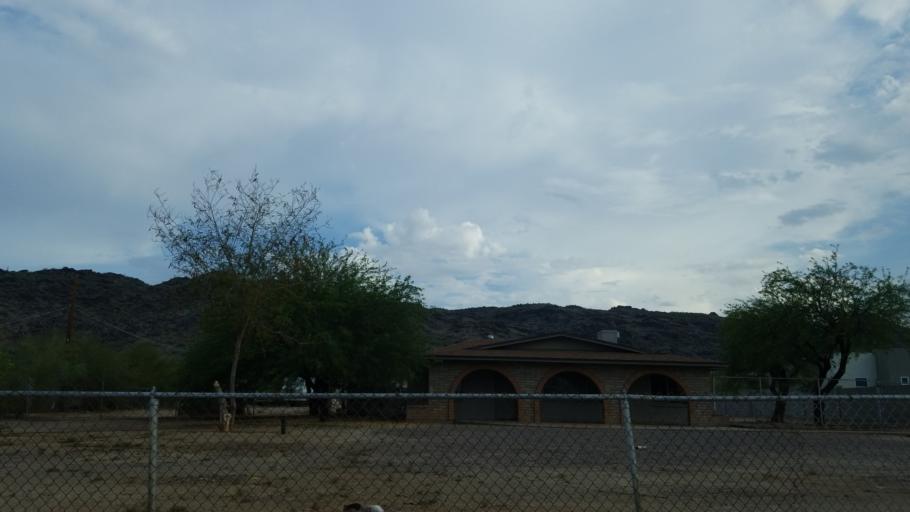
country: US
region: Arizona
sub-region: Maricopa County
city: Guadalupe
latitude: 33.3705
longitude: -112.0296
